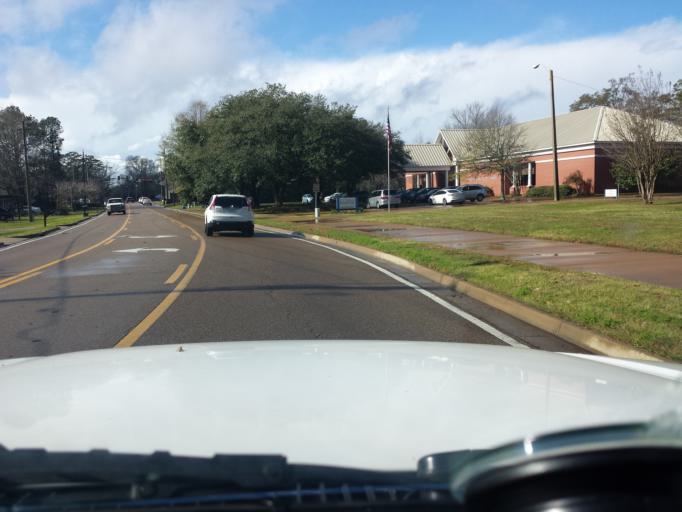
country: US
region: Mississippi
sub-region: Madison County
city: Madison
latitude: 32.4578
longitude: -90.1111
